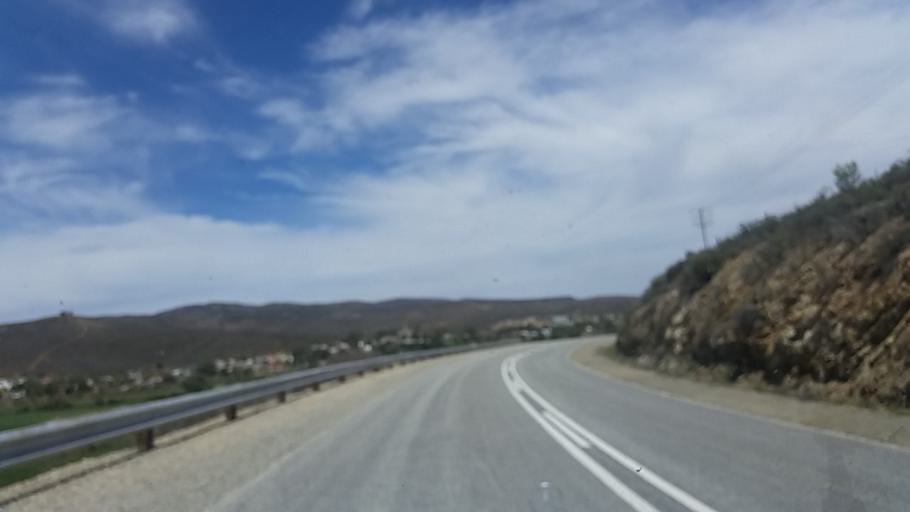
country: ZA
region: Western Cape
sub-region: Eden District Municipality
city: Knysna
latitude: -33.6457
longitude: 23.1329
